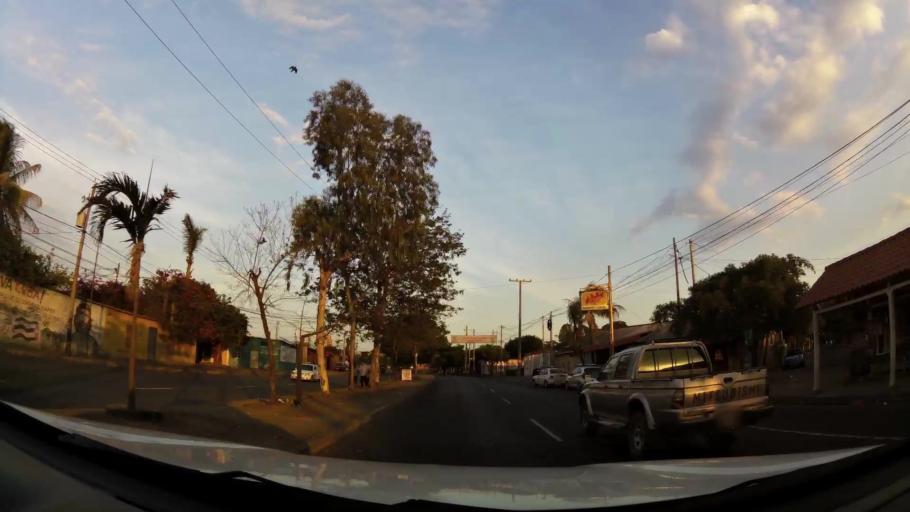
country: NI
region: Managua
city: Managua
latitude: 12.1441
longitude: -86.2268
